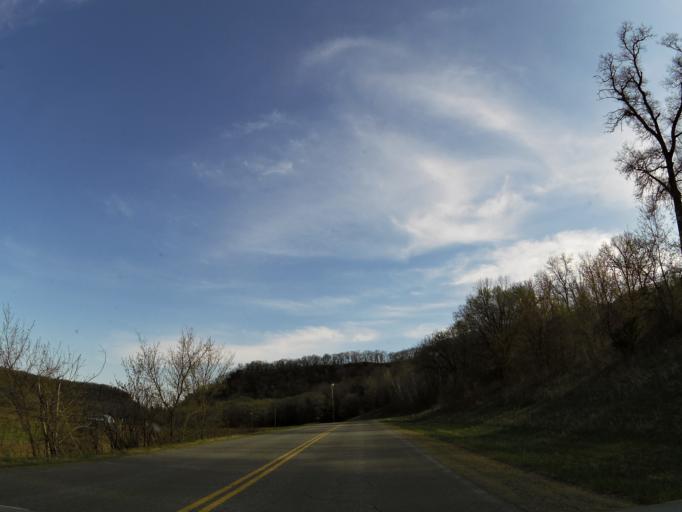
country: US
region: Minnesota
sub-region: Goodhue County
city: Red Wing
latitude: 44.6383
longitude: -92.5834
